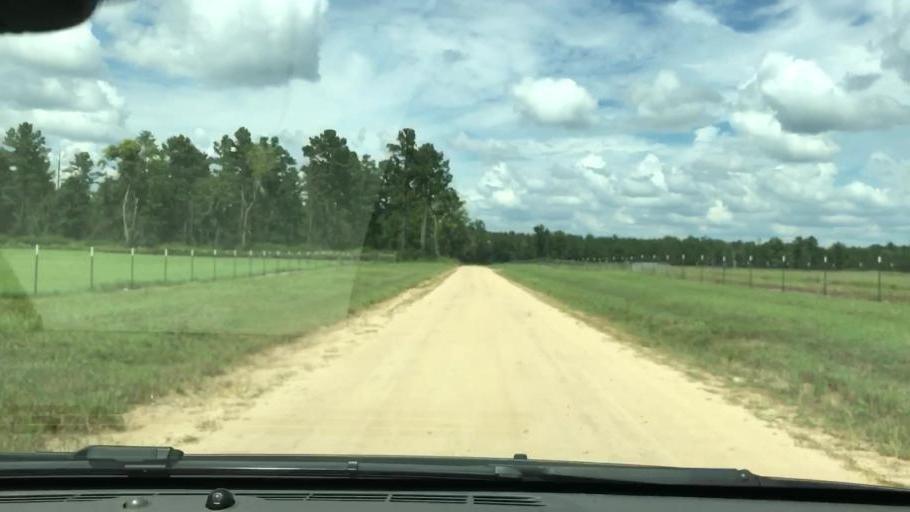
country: US
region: Georgia
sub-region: Quitman County
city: Georgetown
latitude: 32.0323
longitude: -85.0366
